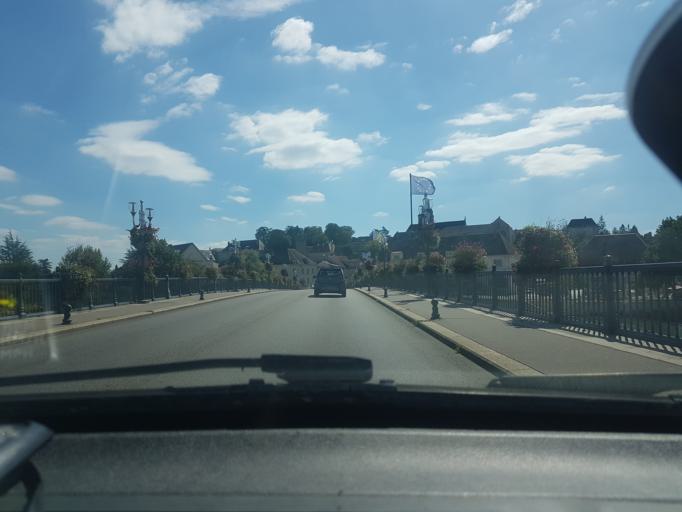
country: FR
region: Franche-Comte
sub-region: Departement de la Haute-Saone
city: Gray
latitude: 47.4500
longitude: 5.5911
